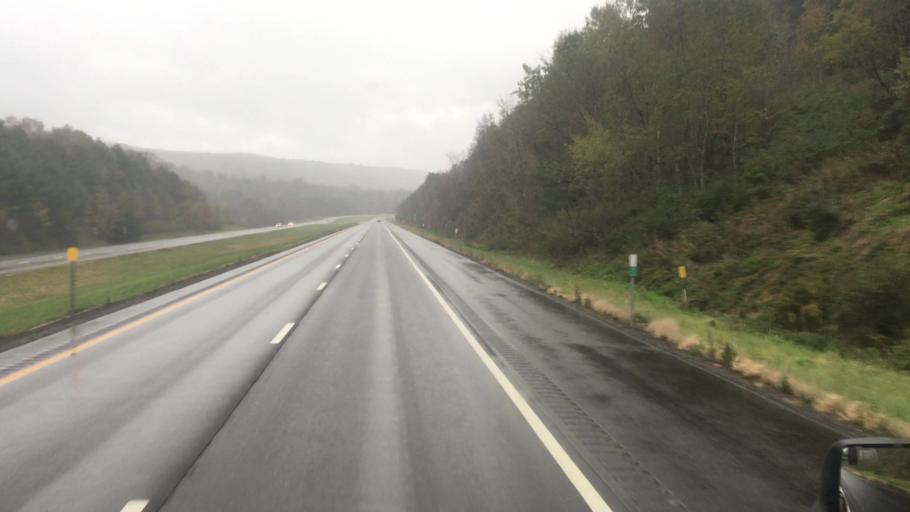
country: US
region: New York
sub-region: Broome County
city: Chenango Bridge
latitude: 42.1765
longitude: -75.7525
